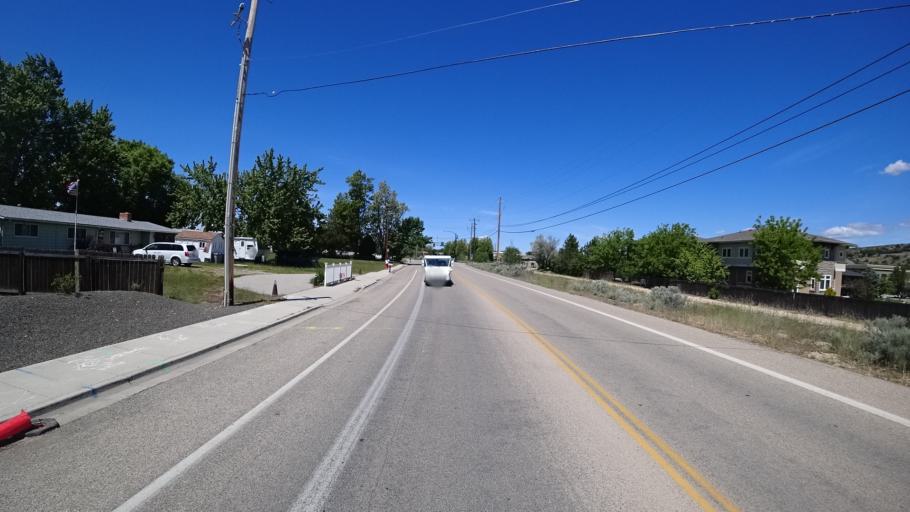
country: US
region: Idaho
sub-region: Ada County
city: Boise
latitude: 43.5725
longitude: -116.1546
